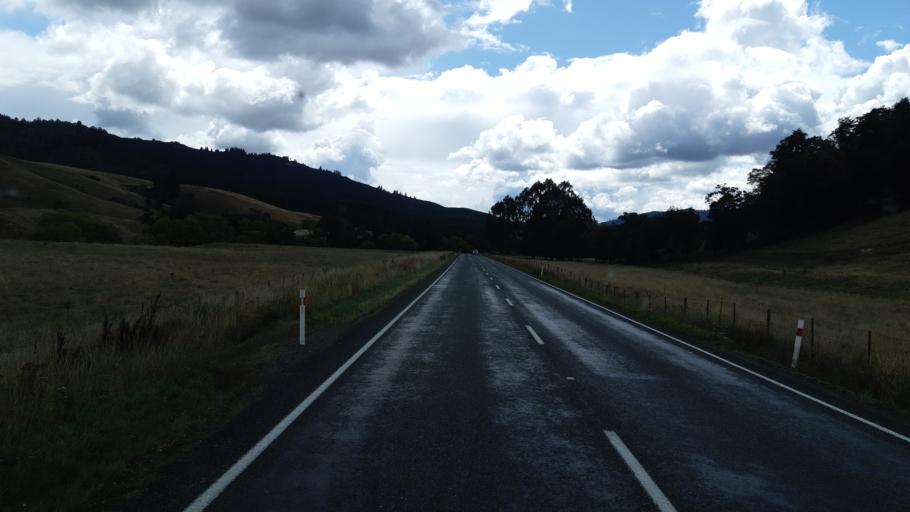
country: NZ
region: Tasman
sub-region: Tasman District
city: Wakefield
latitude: -41.5673
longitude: 172.7771
